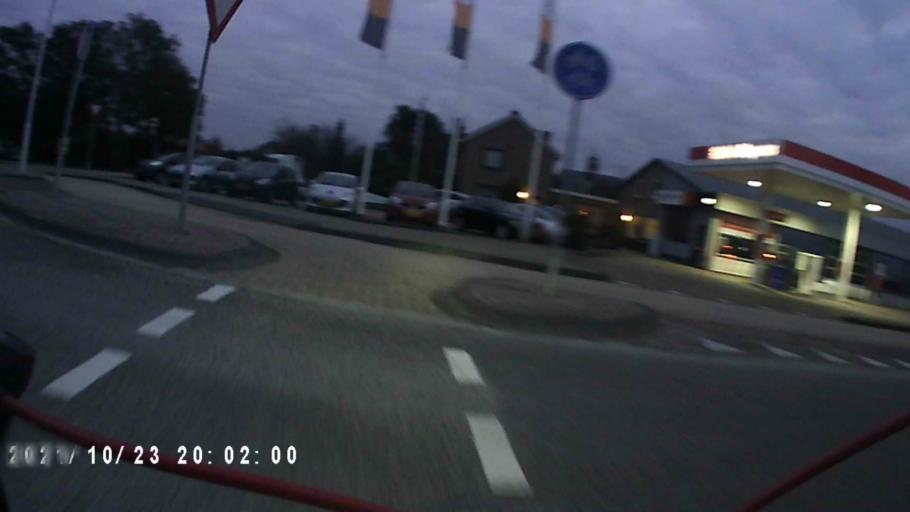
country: NL
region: Friesland
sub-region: Sudwest Fryslan
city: Bolsward
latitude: 53.1043
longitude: 5.4654
